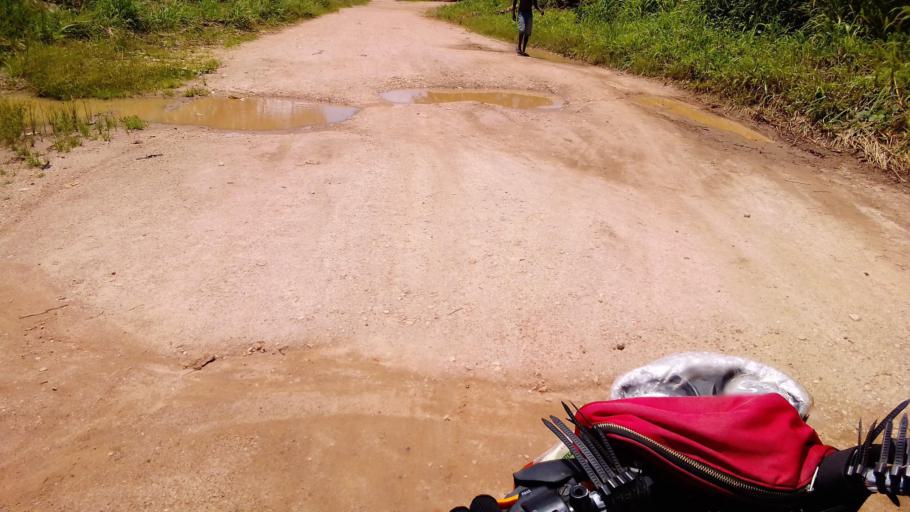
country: SL
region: Eastern Province
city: Koidu
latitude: 8.6667
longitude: -10.9744
